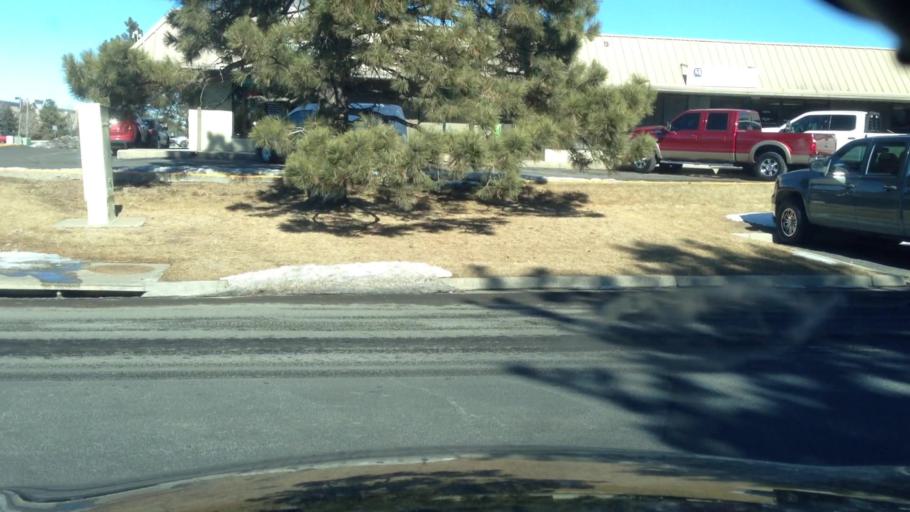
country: US
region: Colorado
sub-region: Douglas County
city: Parker
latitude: 39.5319
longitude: -104.7712
